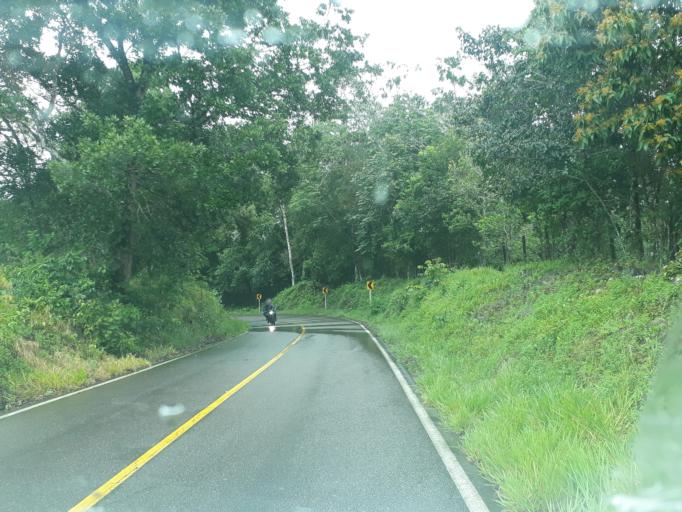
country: CO
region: Cundinamarca
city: Medina
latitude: 4.4535
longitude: -73.3245
